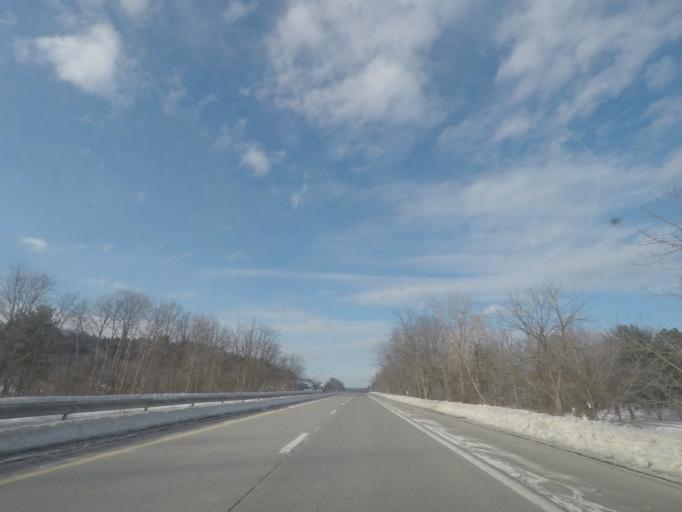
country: US
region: New York
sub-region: Schenectady County
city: Scotia
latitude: 42.8192
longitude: -73.9884
